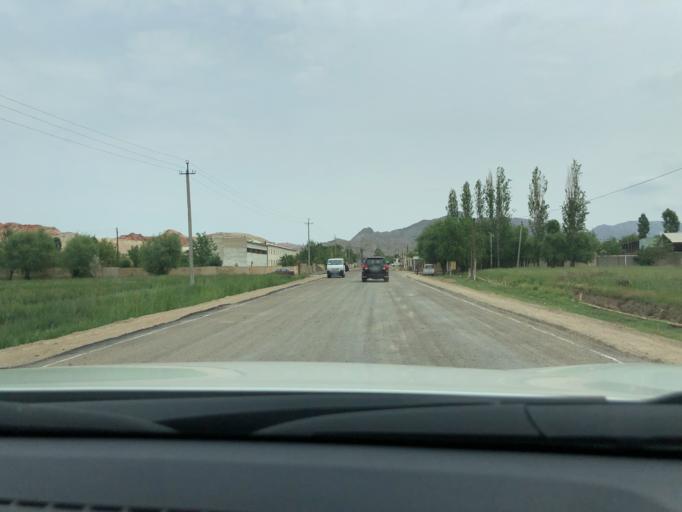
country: TJ
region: Viloyati Sughd
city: Isfara
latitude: 40.1562
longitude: 70.6289
